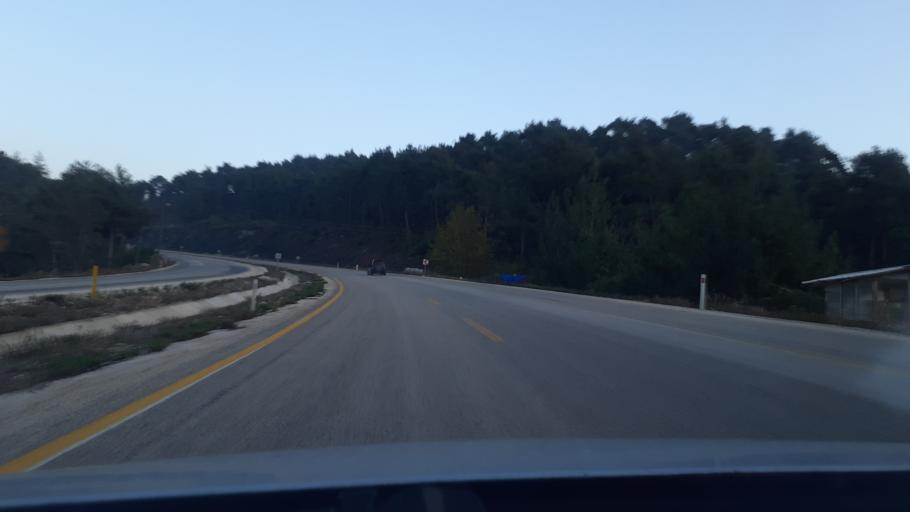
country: TR
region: Hatay
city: Yayladagi
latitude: 35.8915
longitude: 36.0865
